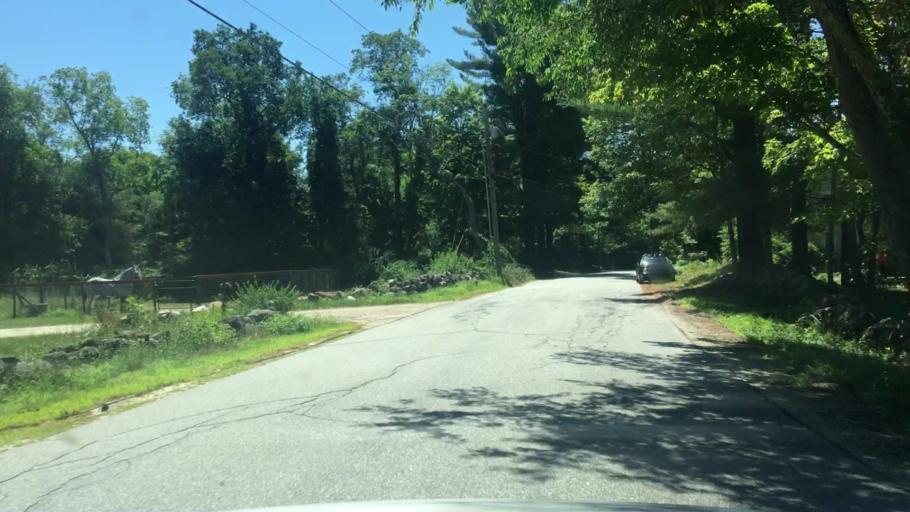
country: US
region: New Hampshire
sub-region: Merrimack County
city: Hopkinton
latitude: 43.2174
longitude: -71.6729
